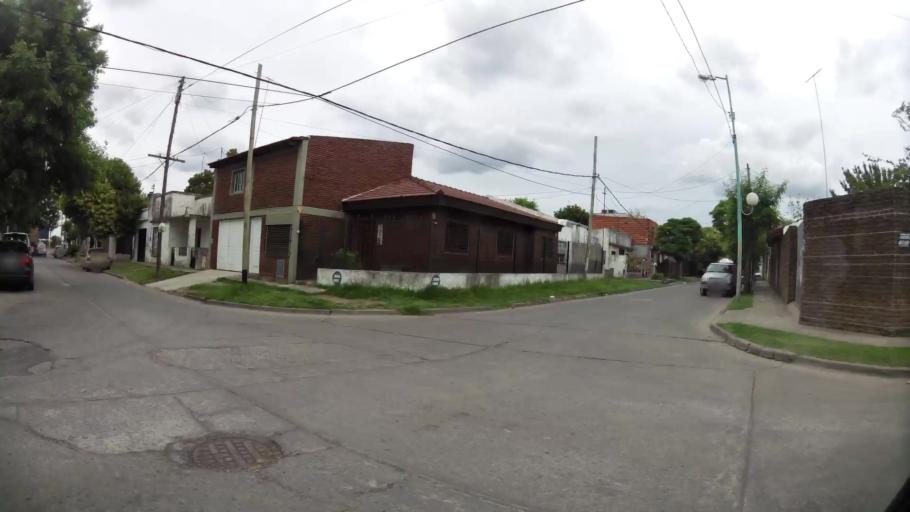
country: AR
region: Buenos Aires
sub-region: Partido de Zarate
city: Zarate
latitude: -34.1120
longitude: -59.0195
